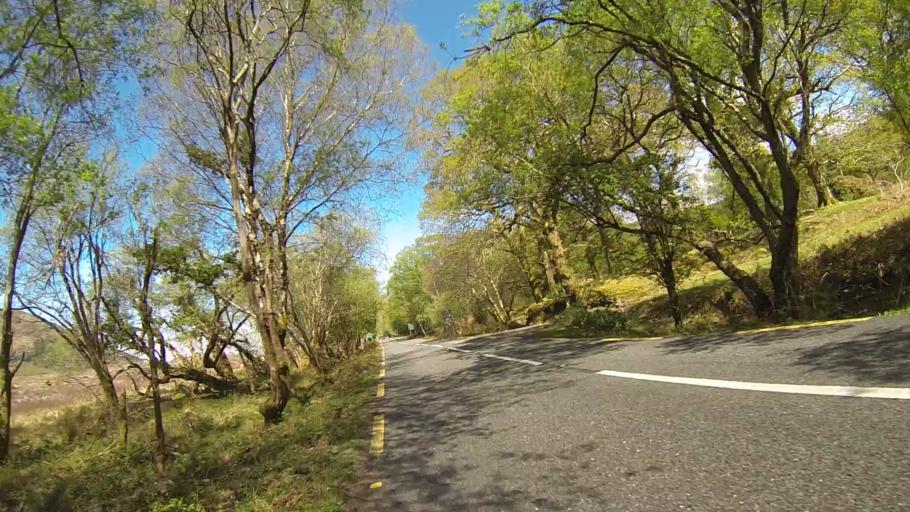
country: IE
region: Munster
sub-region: Ciarrai
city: Cill Airne
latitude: 51.9877
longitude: -9.5585
